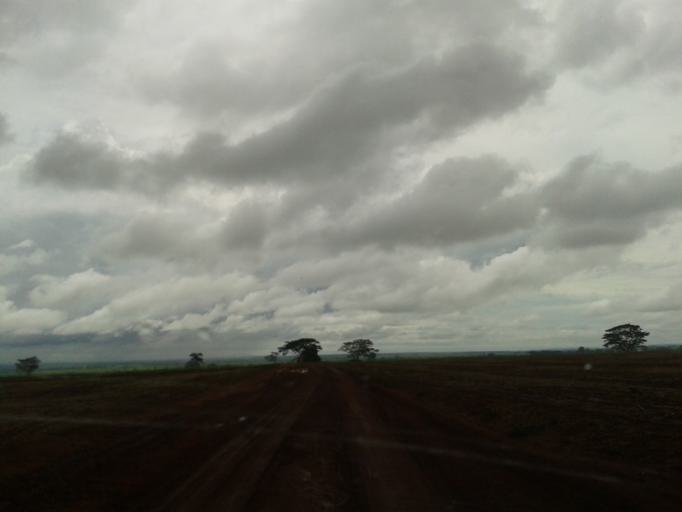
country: BR
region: Minas Gerais
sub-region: Santa Vitoria
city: Santa Vitoria
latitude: -18.6616
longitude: -49.9147
